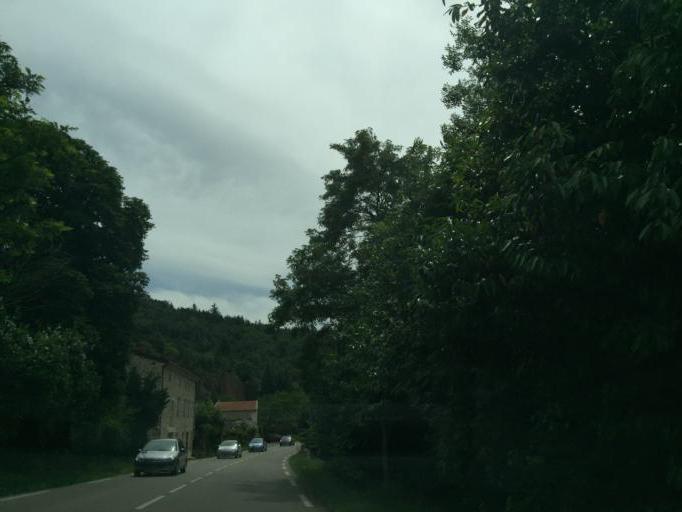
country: FR
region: Rhone-Alpes
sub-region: Departement de l'Ardeche
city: Saint-Marcel-les-Annonay
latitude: 45.2921
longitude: 4.6258
